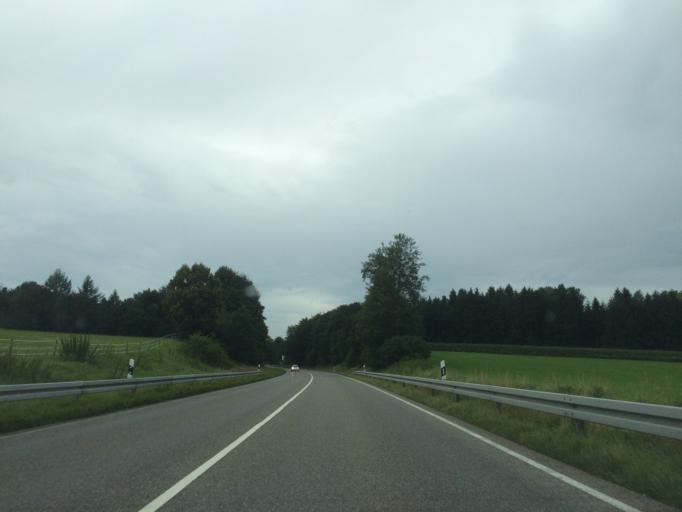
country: DE
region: Baden-Wuerttemberg
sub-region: Tuebingen Region
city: Bad Waldsee
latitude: 47.9239
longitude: 9.7712
